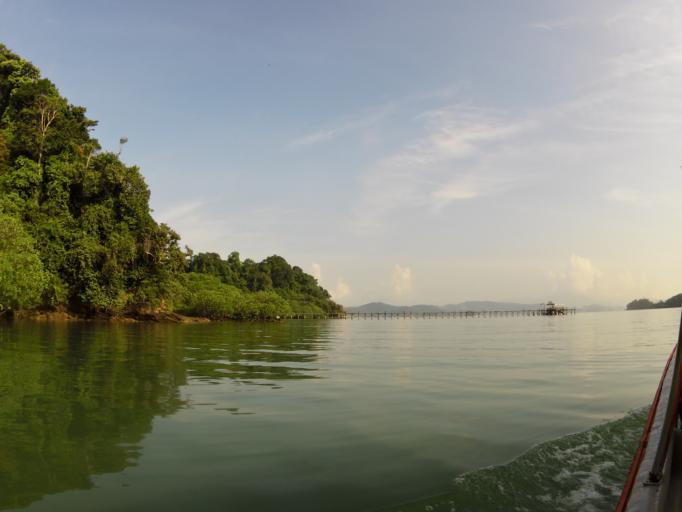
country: MY
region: Kedah
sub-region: Langkawi
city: Kuah
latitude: 6.2239
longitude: 99.7340
